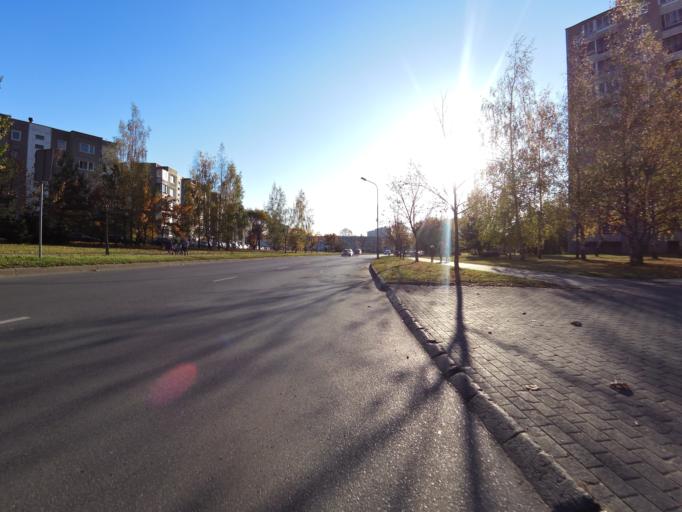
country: LT
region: Vilnius County
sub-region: Vilnius
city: Fabijoniskes
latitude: 54.7360
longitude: 25.2370
